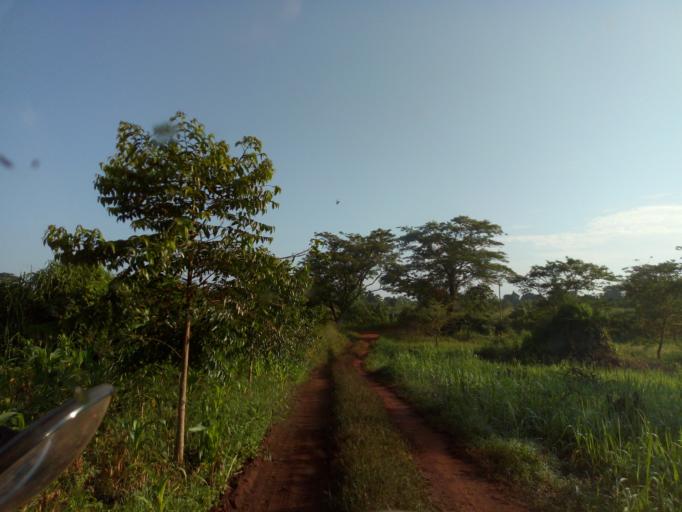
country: UG
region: Western Region
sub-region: Masindi District
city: Masindi
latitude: 1.7752
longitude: 31.8336
